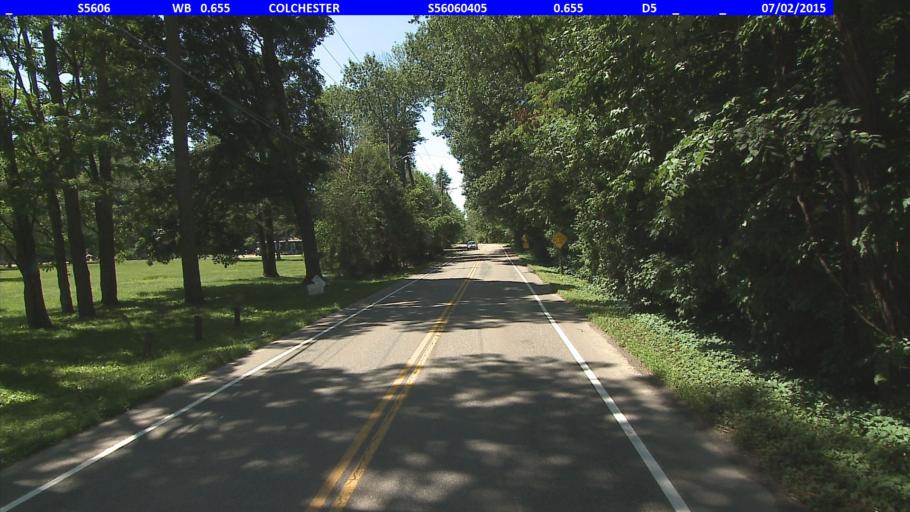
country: US
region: Vermont
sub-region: Chittenden County
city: Winooski
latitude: 44.5527
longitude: -73.2371
